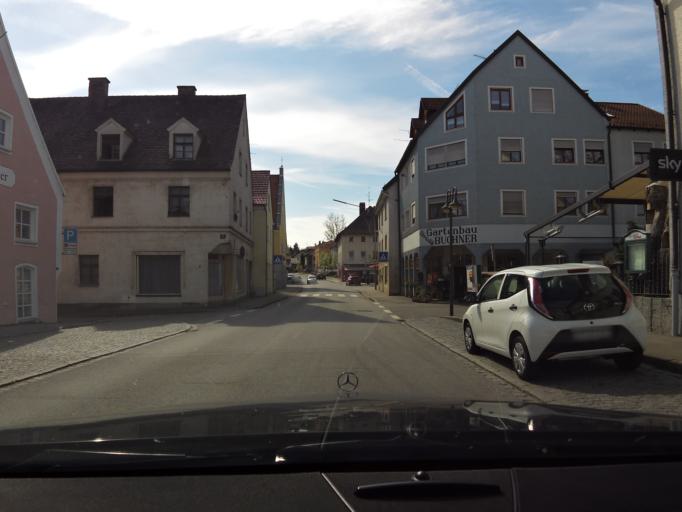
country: DE
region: Bavaria
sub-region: Lower Bavaria
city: Mallersdorf-Pfaffenberg
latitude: 48.7692
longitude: 12.2272
